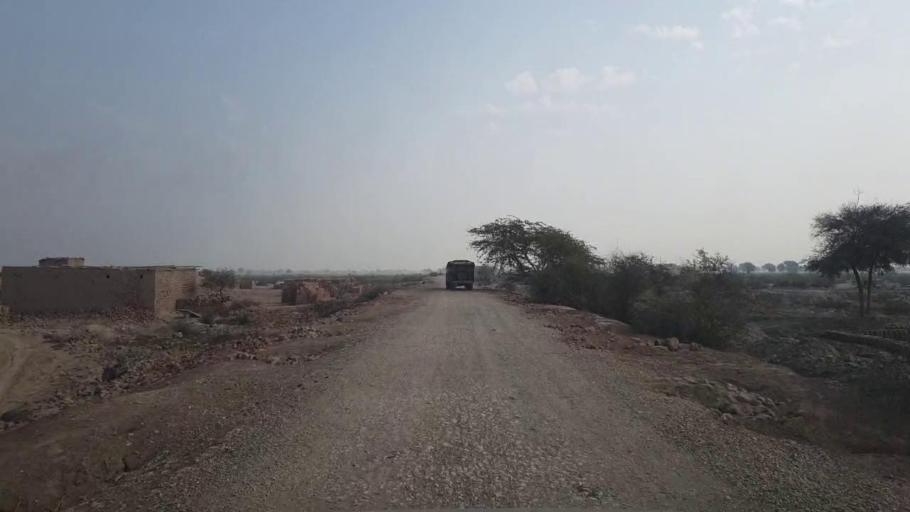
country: PK
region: Sindh
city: Hala
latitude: 25.7646
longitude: 68.4184
